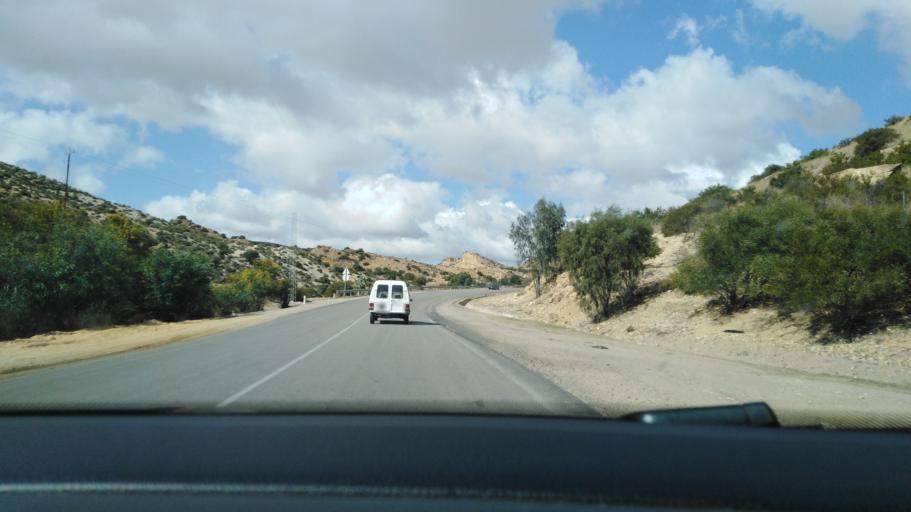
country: TN
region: Al Qayrawan
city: Haffouz
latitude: 35.6347
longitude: 9.8197
